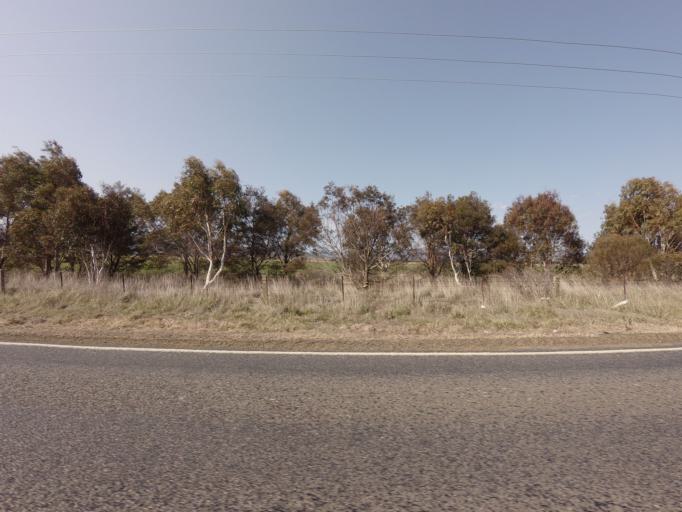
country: AU
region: Tasmania
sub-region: Northern Midlands
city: Evandale
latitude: -41.7898
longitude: 147.7127
